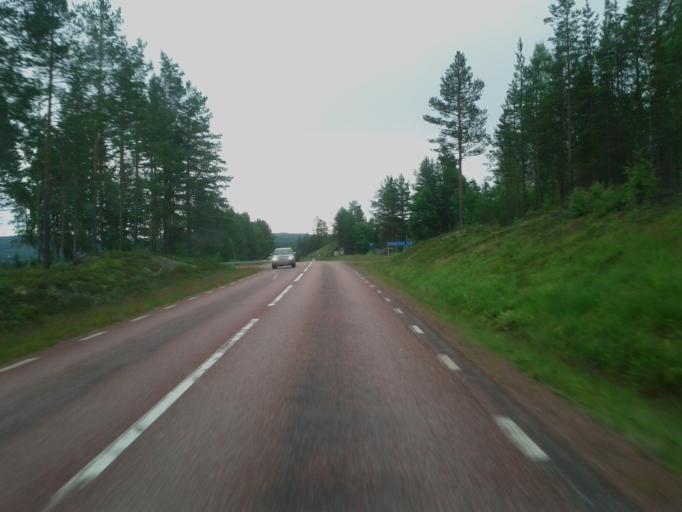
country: SE
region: Dalarna
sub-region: Alvdalens Kommun
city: AElvdalen
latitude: 61.2832
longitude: 13.7561
